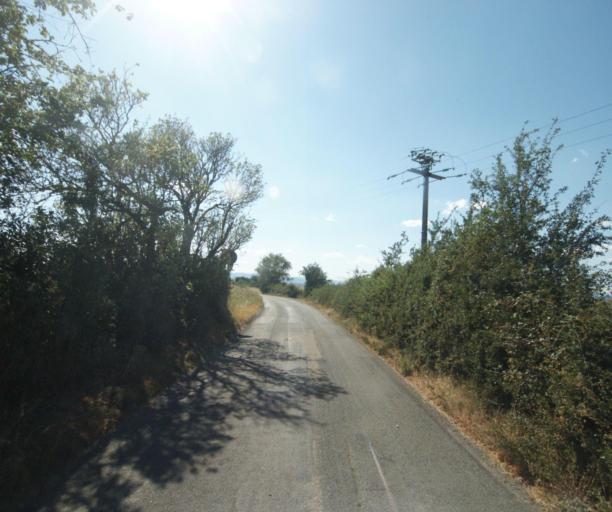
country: FR
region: Rhone-Alpes
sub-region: Departement du Rhone
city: La Tour-de-Salvagny
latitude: 45.8267
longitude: 4.7347
